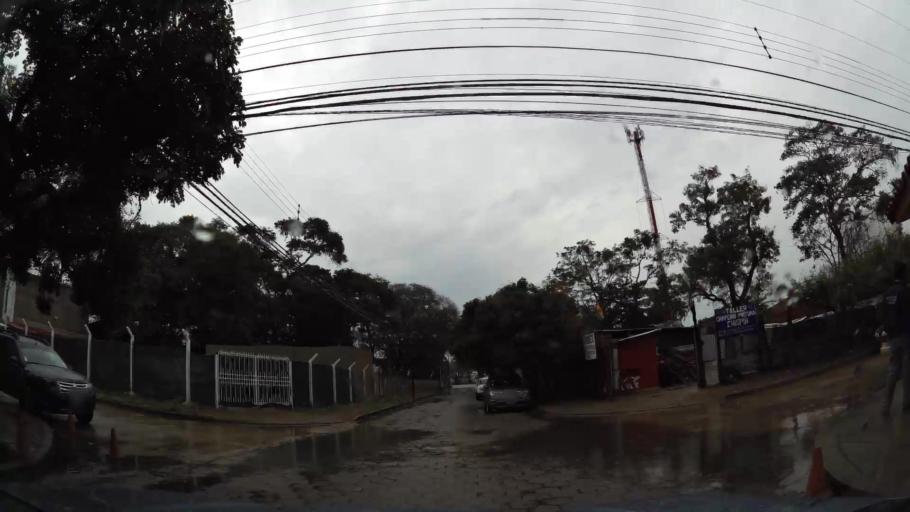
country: BO
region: Santa Cruz
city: Santa Cruz de la Sierra
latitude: -17.7866
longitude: -63.2080
